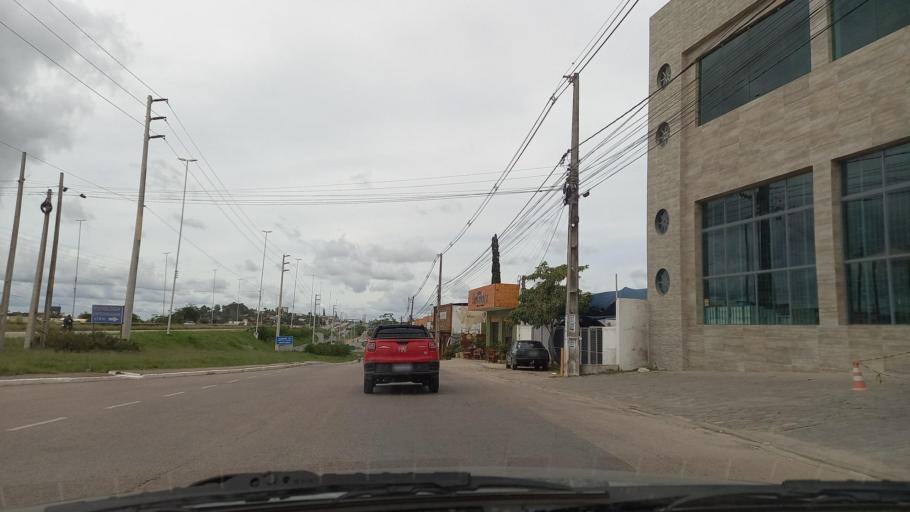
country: BR
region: Pernambuco
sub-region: Gravata
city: Gravata
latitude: -8.1955
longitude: -35.5641
